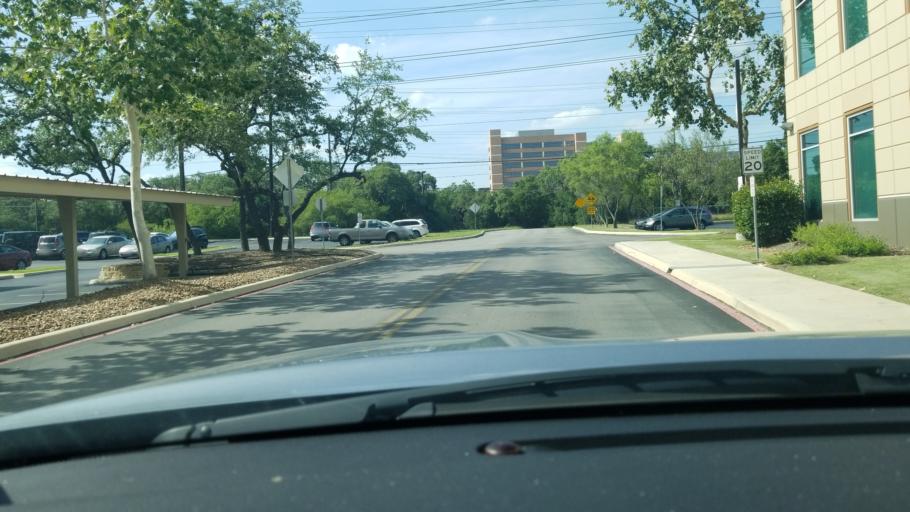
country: US
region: Texas
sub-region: Bexar County
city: Hollywood Park
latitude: 29.6170
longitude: -98.4911
